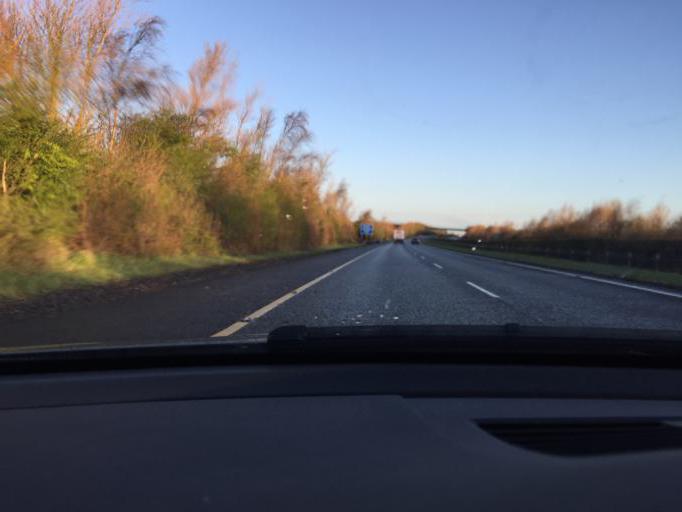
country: IE
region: Leinster
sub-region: An Mhi
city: Stamullin
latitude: 53.6123
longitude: -6.2394
